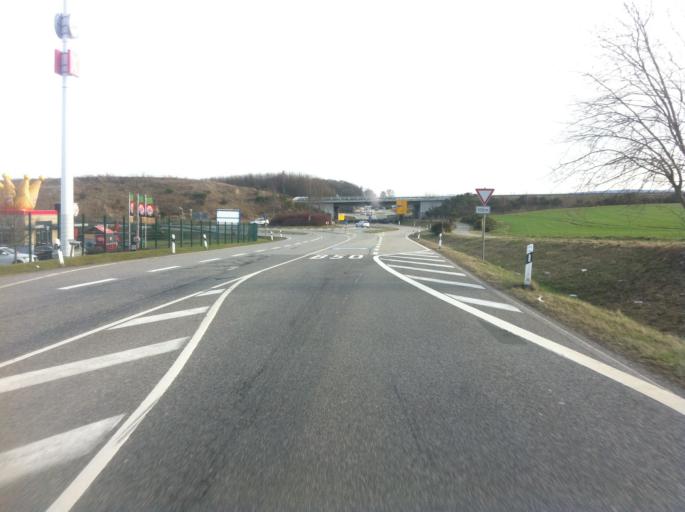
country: DE
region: Rheinland-Pfalz
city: Lautzenhausen
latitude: 49.9305
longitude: 7.2768
